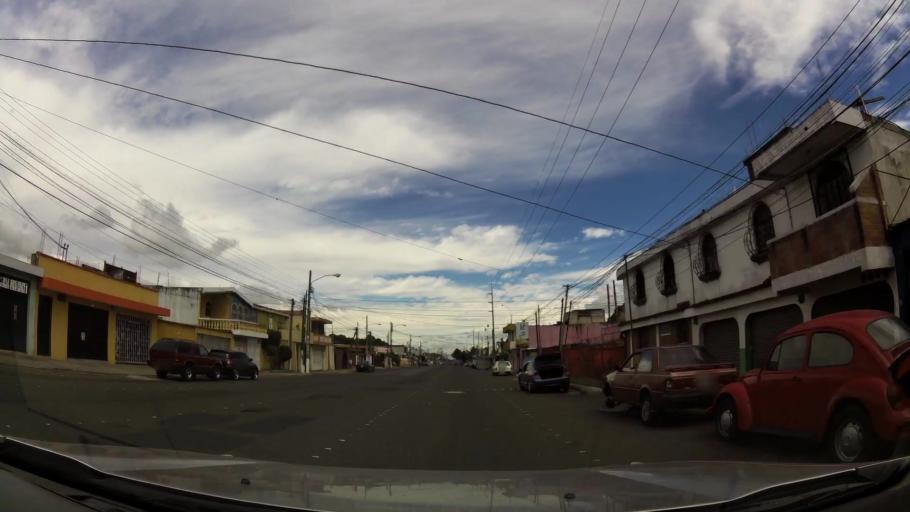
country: GT
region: Guatemala
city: Mixco
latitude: 14.6412
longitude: -90.5810
